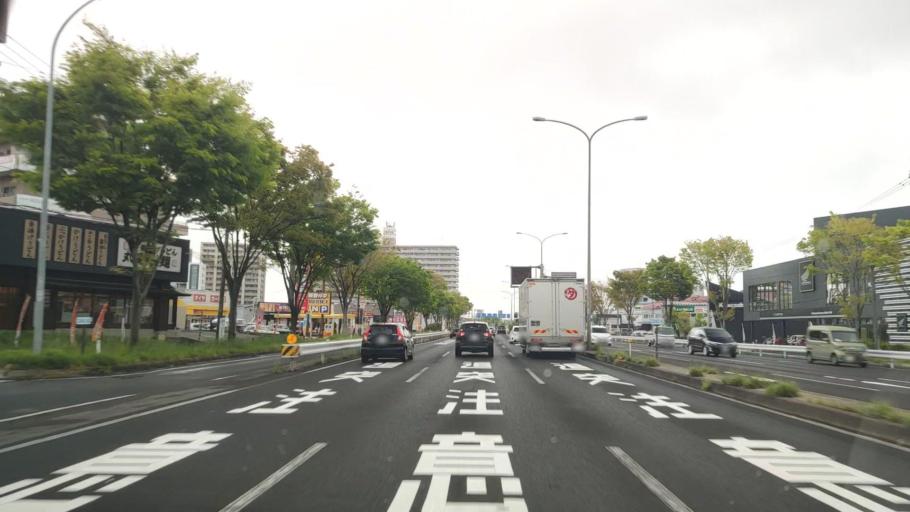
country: JP
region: Miyagi
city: Sendai-shi
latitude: 38.2468
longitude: 140.9244
